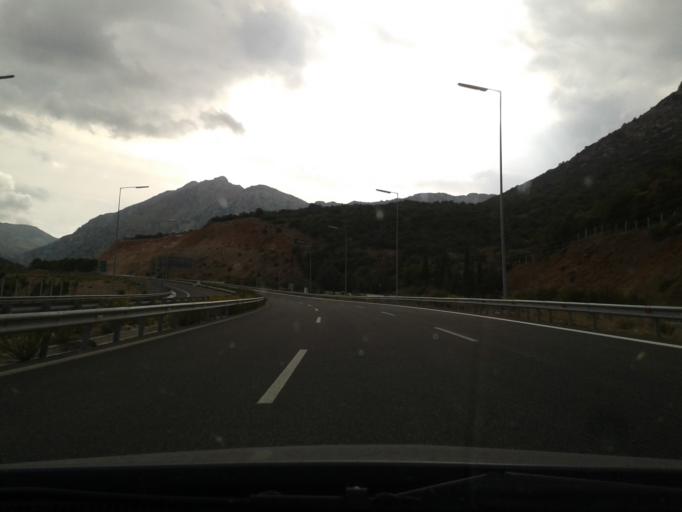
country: GR
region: Peloponnese
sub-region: Nomos Arkadias
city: Tripoli
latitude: 37.6790
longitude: 22.4889
